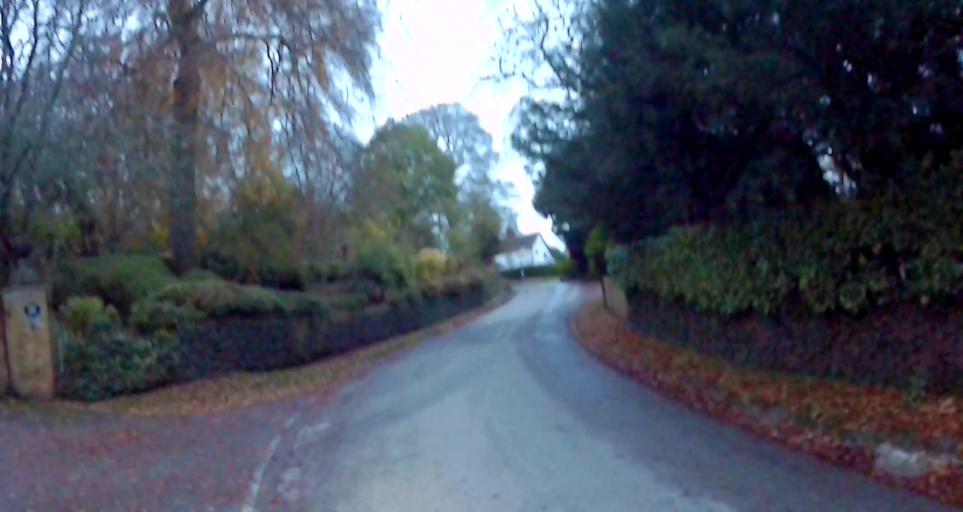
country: GB
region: England
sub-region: Hampshire
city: Old Basing
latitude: 51.2312
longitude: -1.0033
